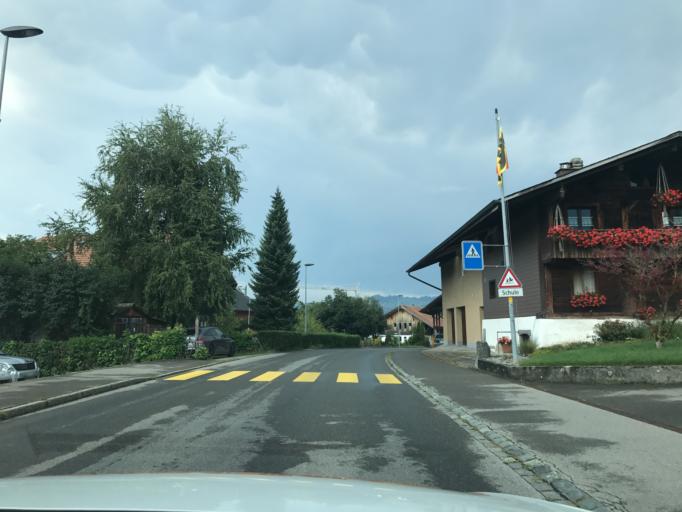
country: CH
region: Bern
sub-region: Thun District
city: Thierachern
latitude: 46.7272
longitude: 7.5800
